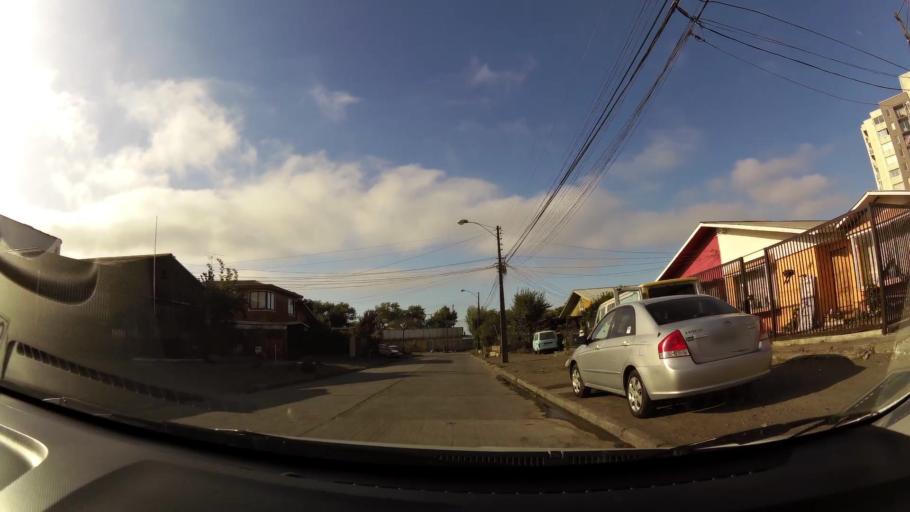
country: CL
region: Biobio
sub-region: Provincia de Concepcion
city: Concepcion
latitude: -36.7874
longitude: -73.0916
